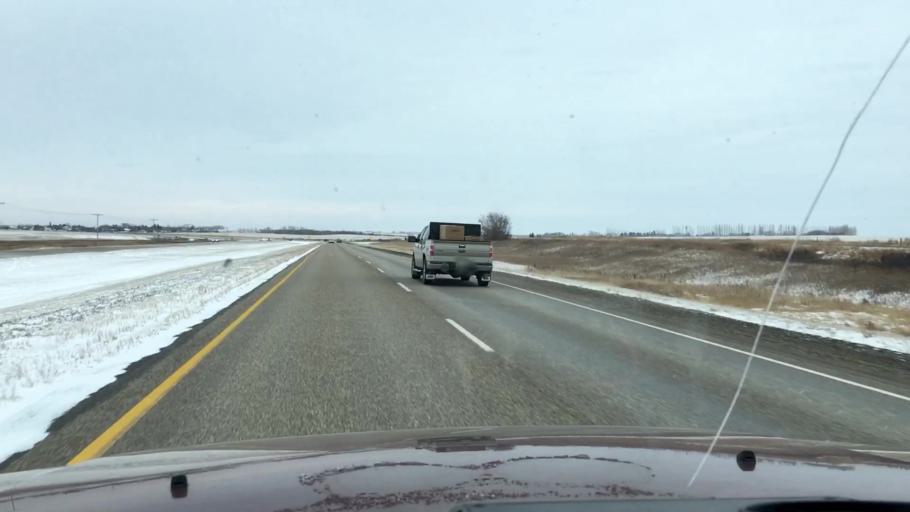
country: CA
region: Saskatchewan
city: Moose Jaw
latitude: 50.9549
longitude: -105.7104
